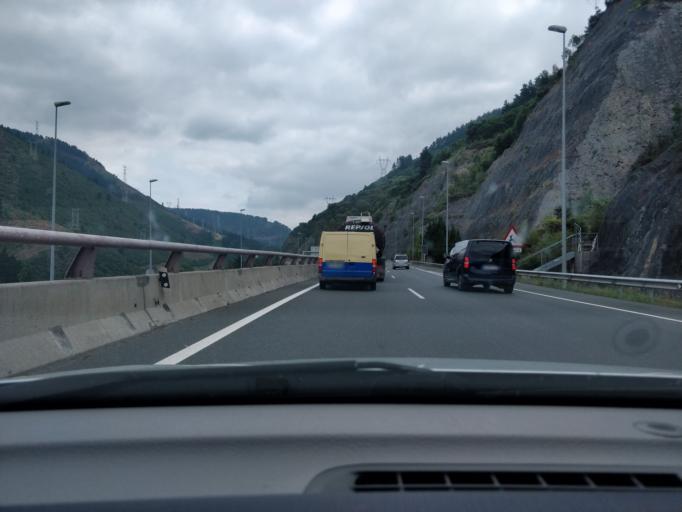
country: ES
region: Basque Country
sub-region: Bizkaia
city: Gordexola
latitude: 43.2074
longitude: -3.0414
